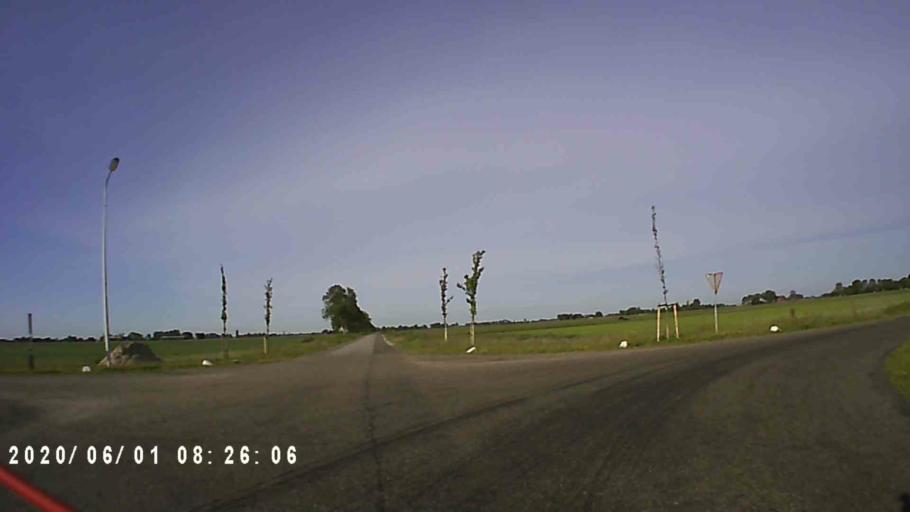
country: NL
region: Friesland
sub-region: Gemeente Ferwerderadiel
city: Burdaard
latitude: 53.2986
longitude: 5.8628
